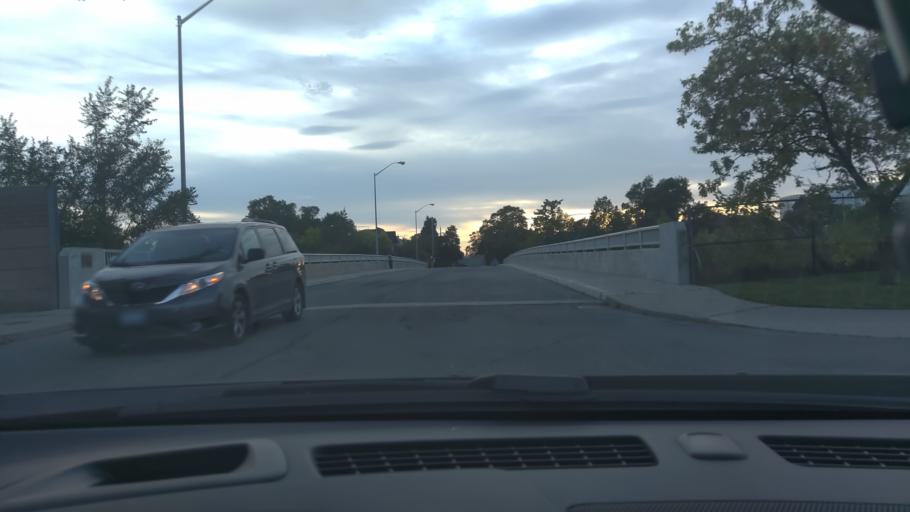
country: CA
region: Ontario
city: Toronto
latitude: 43.7149
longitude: -79.4427
